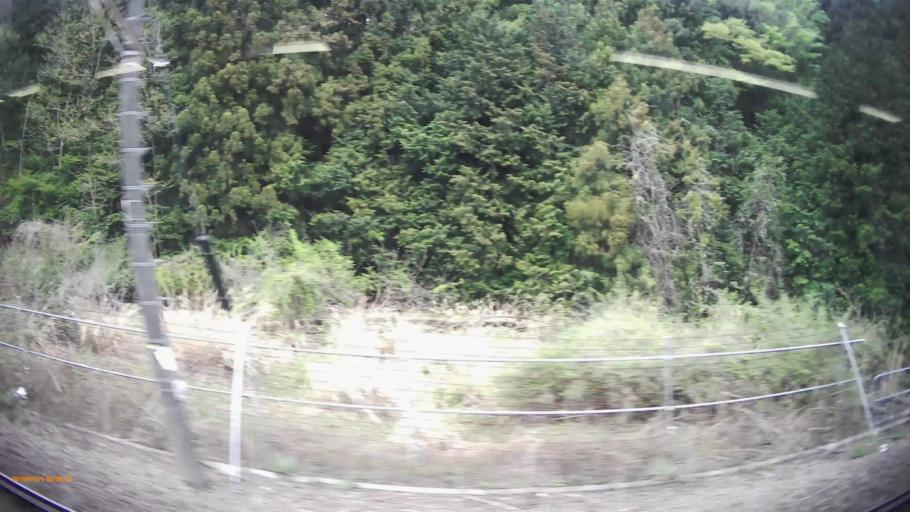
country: JP
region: Yamanashi
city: Otsuki
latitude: 35.6057
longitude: 138.8363
